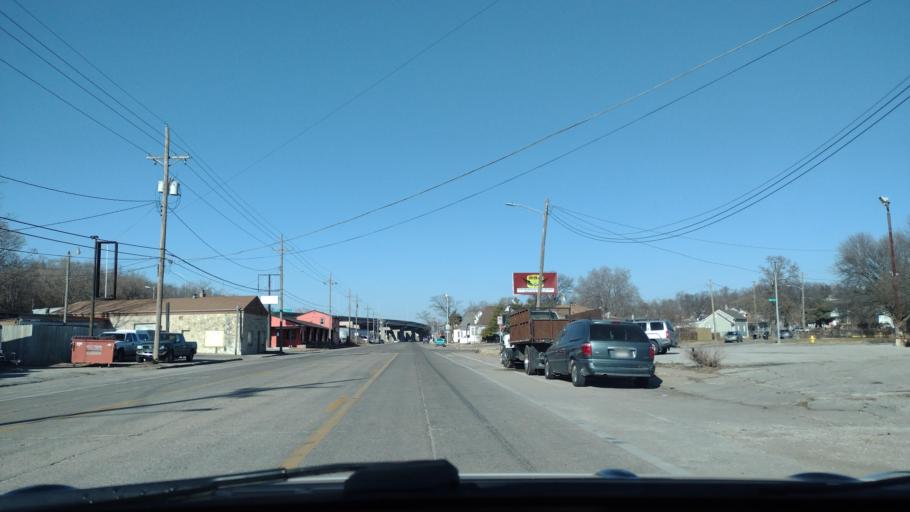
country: US
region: Nebraska
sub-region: Douglas County
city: Omaha
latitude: 41.1923
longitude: -95.9381
